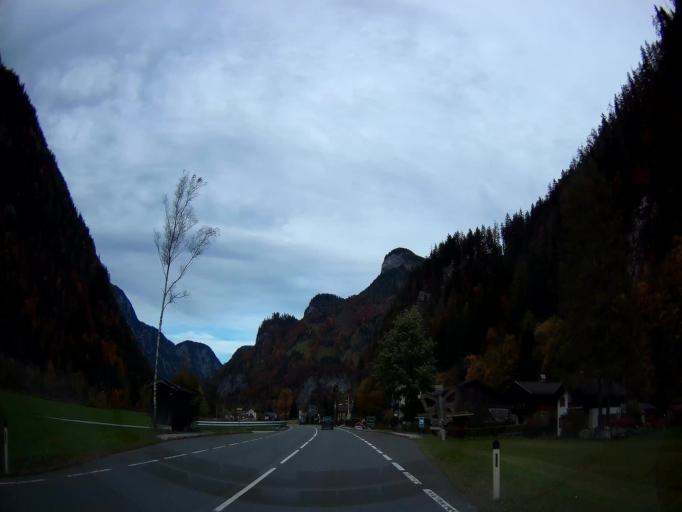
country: AT
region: Salzburg
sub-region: Politischer Bezirk Zell am See
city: Leogang
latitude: 47.5146
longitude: 12.7589
